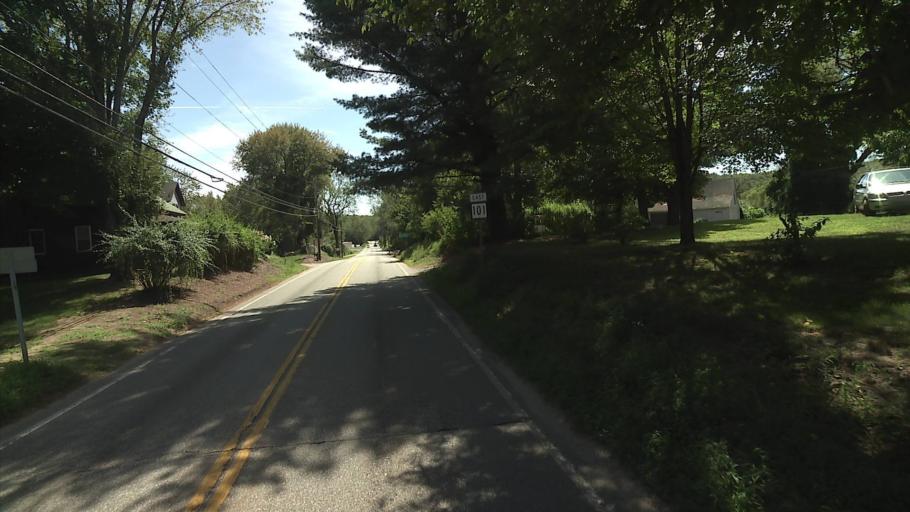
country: US
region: Connecticut
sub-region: Windham County
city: Putnam
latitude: 41.8577
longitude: -71.9587
